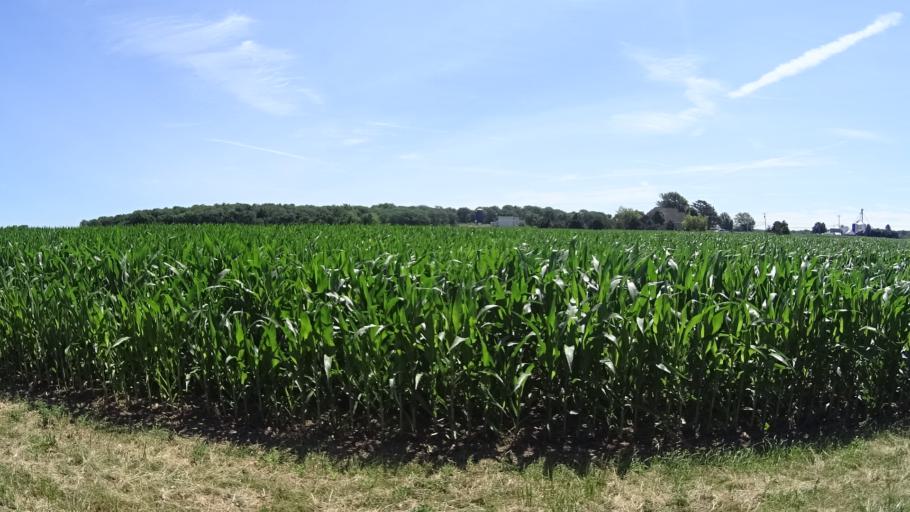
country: US
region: Ohio
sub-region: Ottawa County
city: Port Clinton
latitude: 41.4387
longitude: -82.8527
